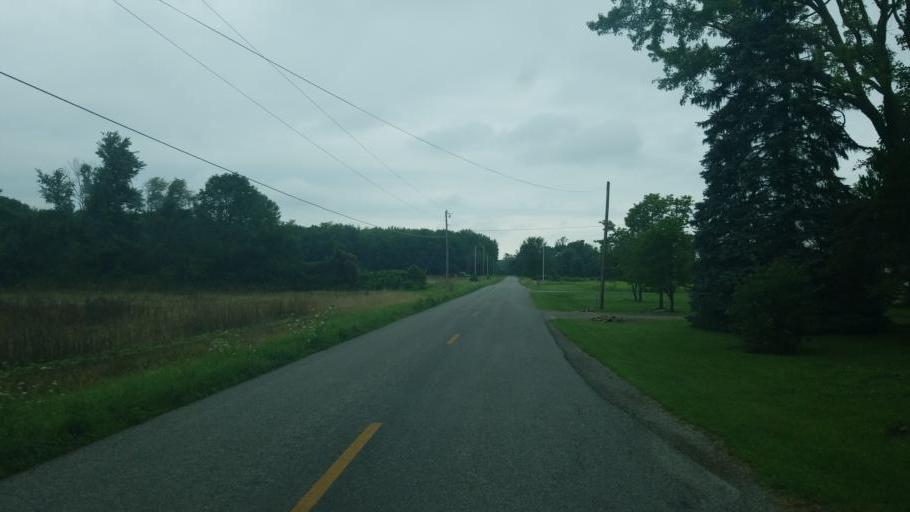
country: US
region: Ohio
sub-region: Delaware County
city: Sunbury
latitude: 40.3149
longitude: -82.8671
